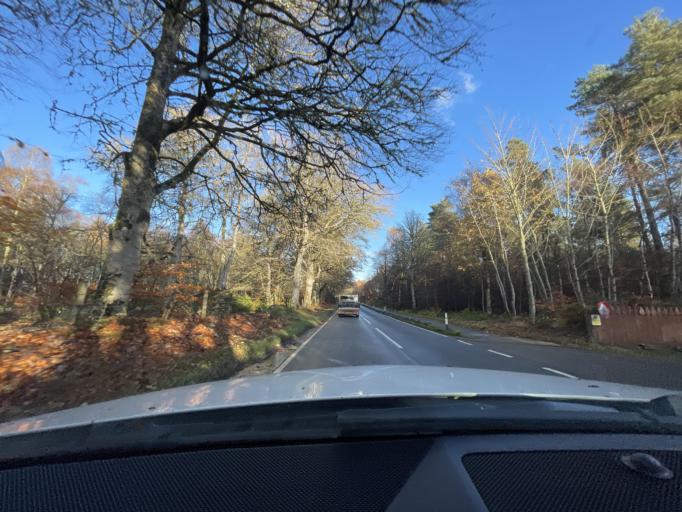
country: GB
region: Scotland
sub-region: Highland
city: Inverness
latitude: 57.4358
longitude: -4.2696
